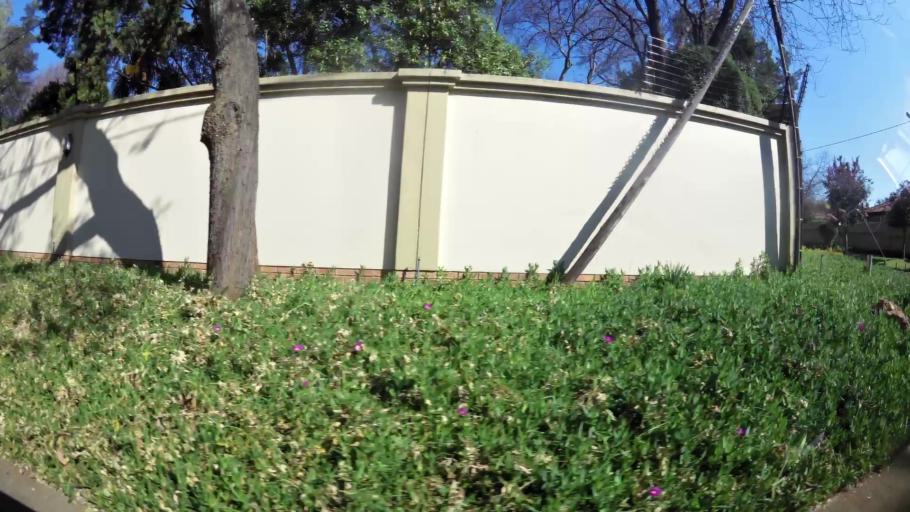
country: ZA
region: Gauteng
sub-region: City of Johannesburg Metropolitan Municipality
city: Johannesburg
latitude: -26.0970
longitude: 28.0284
